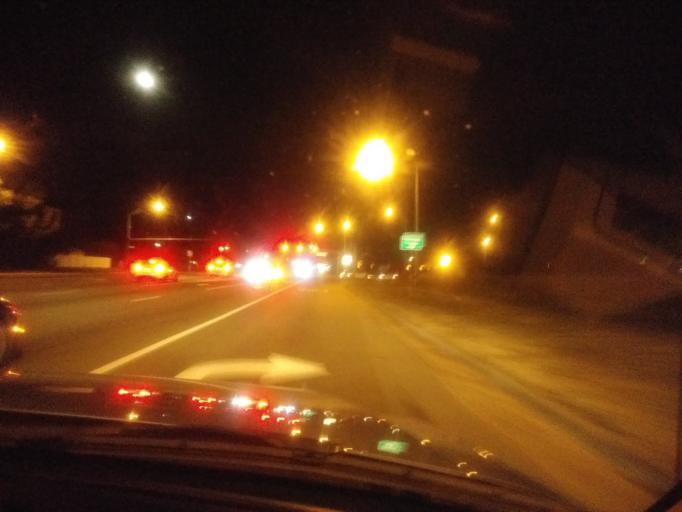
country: US
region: Virginia
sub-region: City of Chesapeake
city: Chesapeake
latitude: 36.8037
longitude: -76.1881
